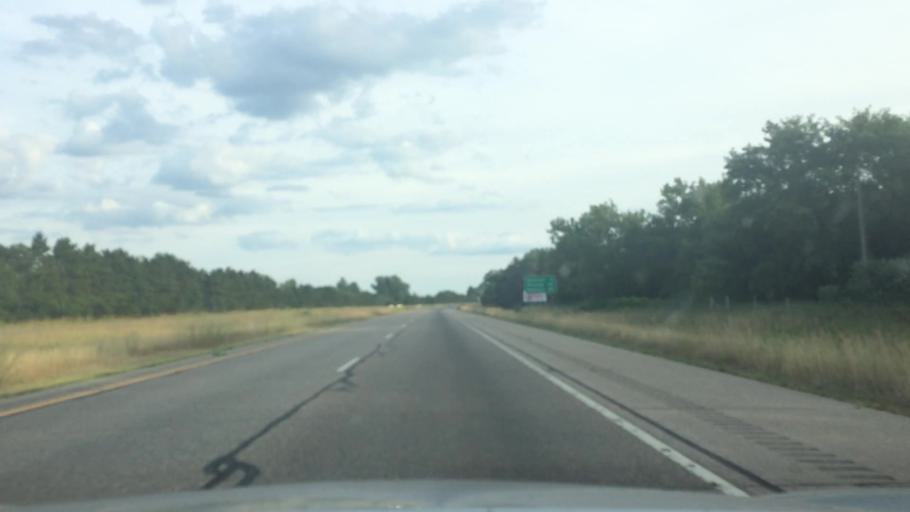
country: US
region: Wisconsin
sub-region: Portage County
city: Plover
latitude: 44.2022
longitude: -89.5233
